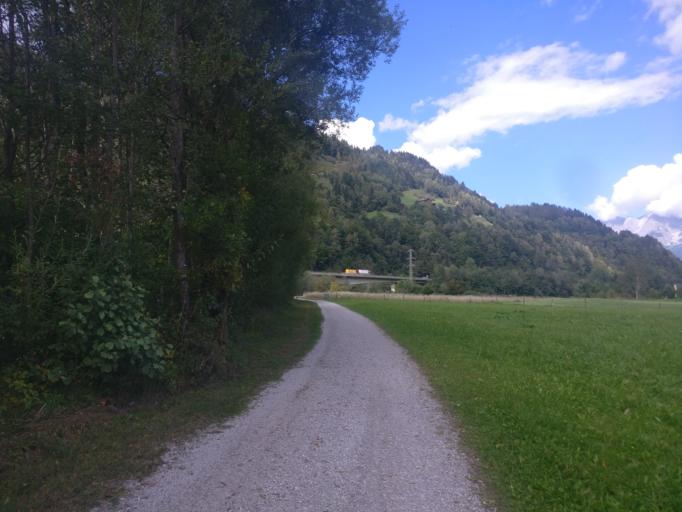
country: AT
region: Salzburg
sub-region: Politischer Bezirk Sankt Johann im Pongau
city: Sankt Johann im Pongau
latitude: 47.3815
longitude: 13.2138
